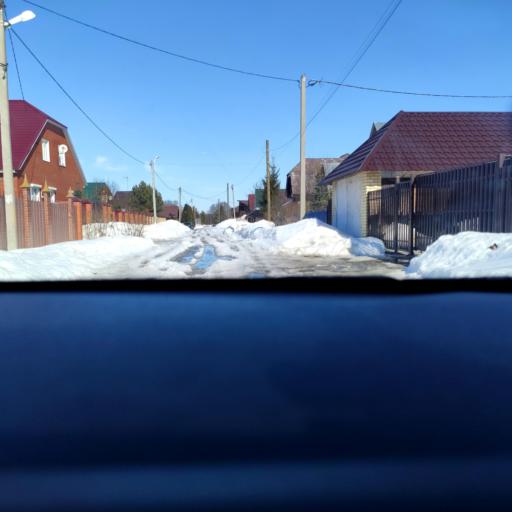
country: RU
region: Tatarstan
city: Laishevo
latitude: 55.6055
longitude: 49.4471
